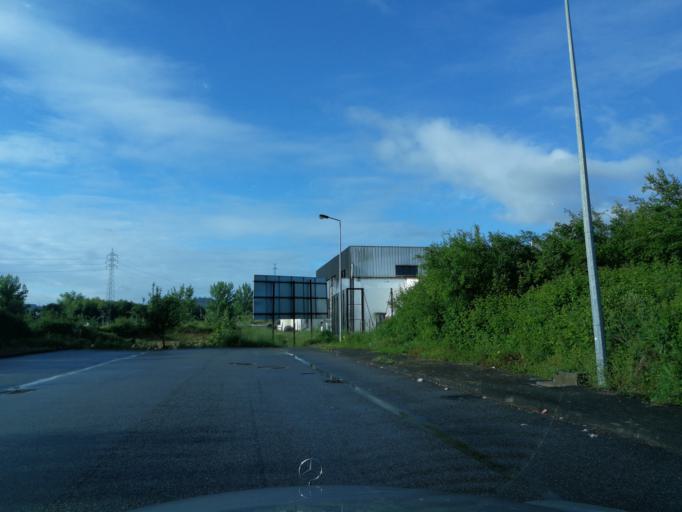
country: PT
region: Braga
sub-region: Braga
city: Braga
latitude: 41.5667
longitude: -8.4477
